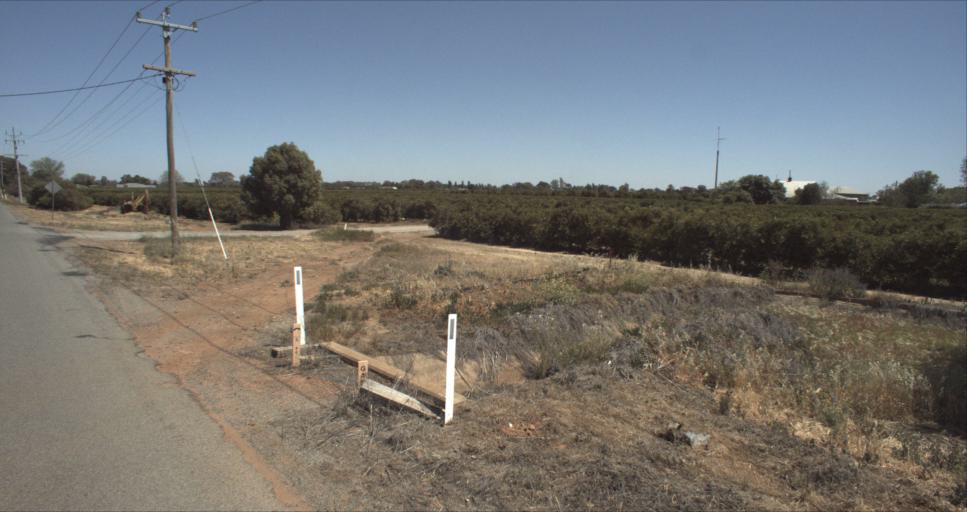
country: AU
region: New South Wales
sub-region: Leeton
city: Leeton
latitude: -34.5348
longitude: 146.3983
